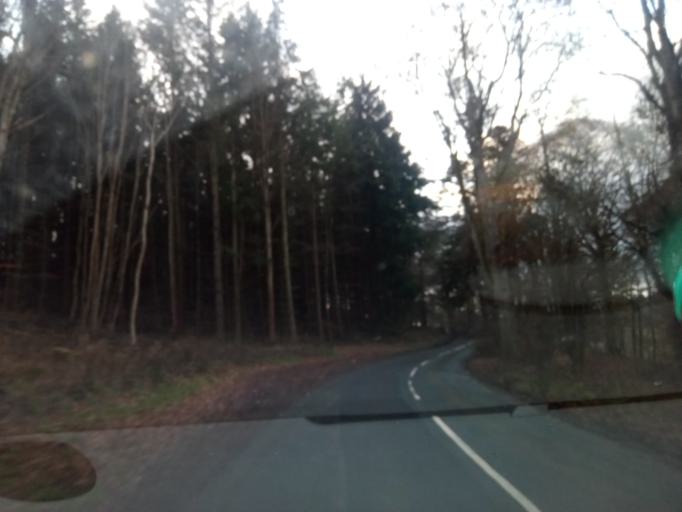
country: GB
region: Scotland
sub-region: The Scottish Borders
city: Galashiels
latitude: 55.5940
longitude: -2.7887
